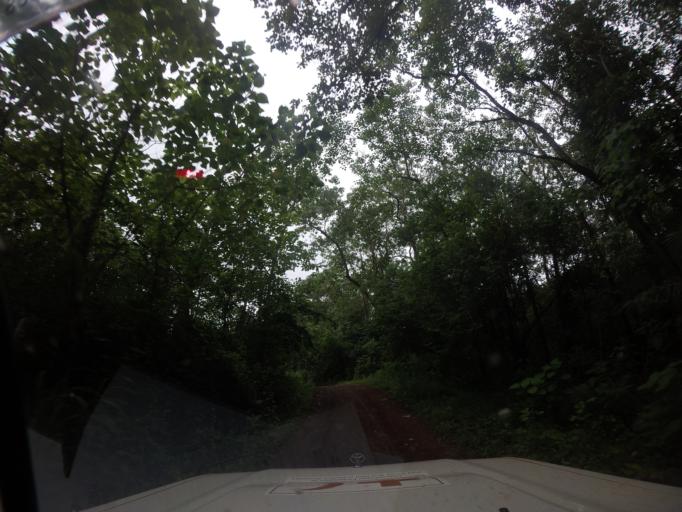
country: SL
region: Northern Province
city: Kamakwie
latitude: 9.6165
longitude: -12.2143
